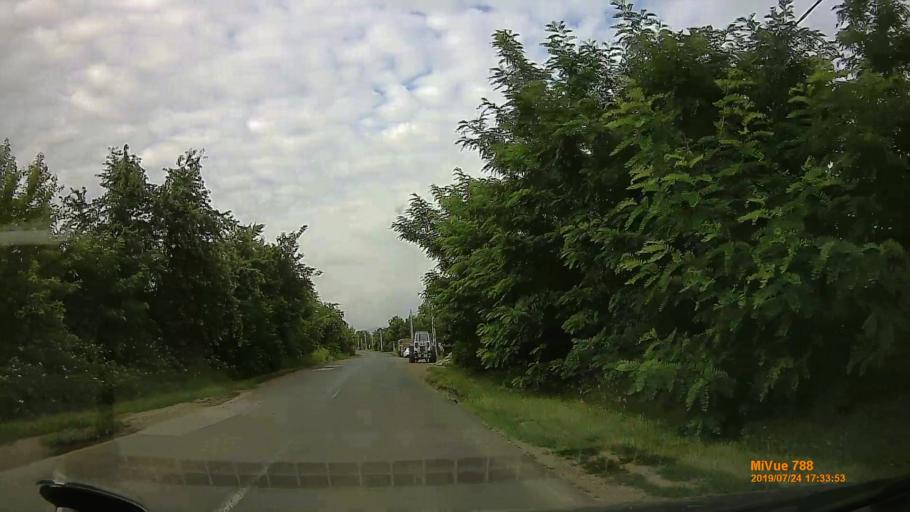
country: HU
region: Borsod-Abauj-Zemplen
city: Abaujszanto
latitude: 48.2988
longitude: 21.1945
